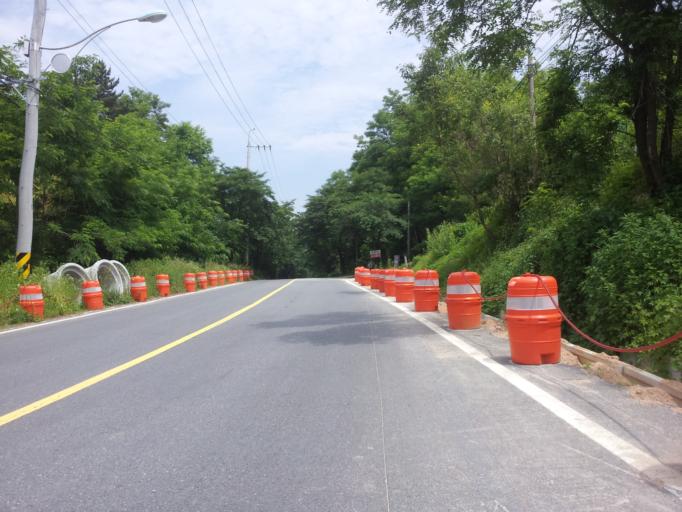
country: KR
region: Chungcheongbuk-do
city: Okcheon
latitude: 36.3823
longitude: 127.5188
